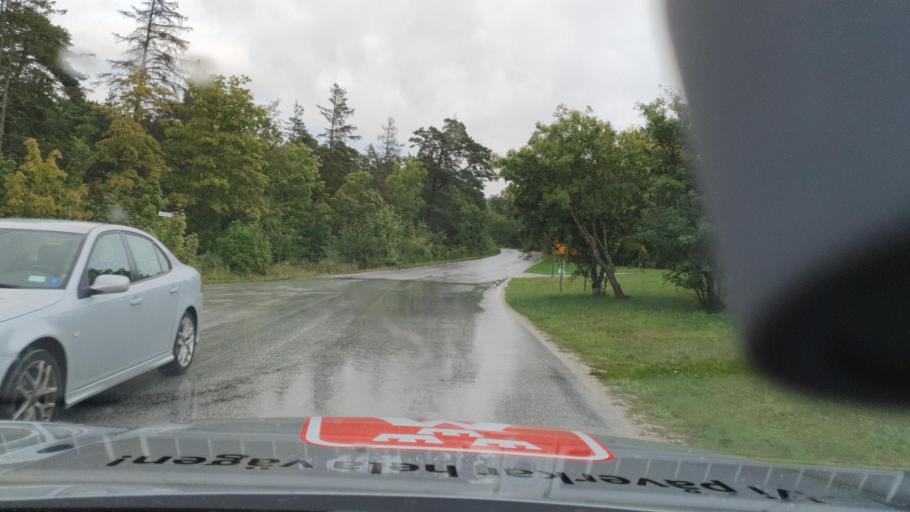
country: SE
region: Gotland
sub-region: Gotland
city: Vibble
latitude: 57.5971
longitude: 18.2112
